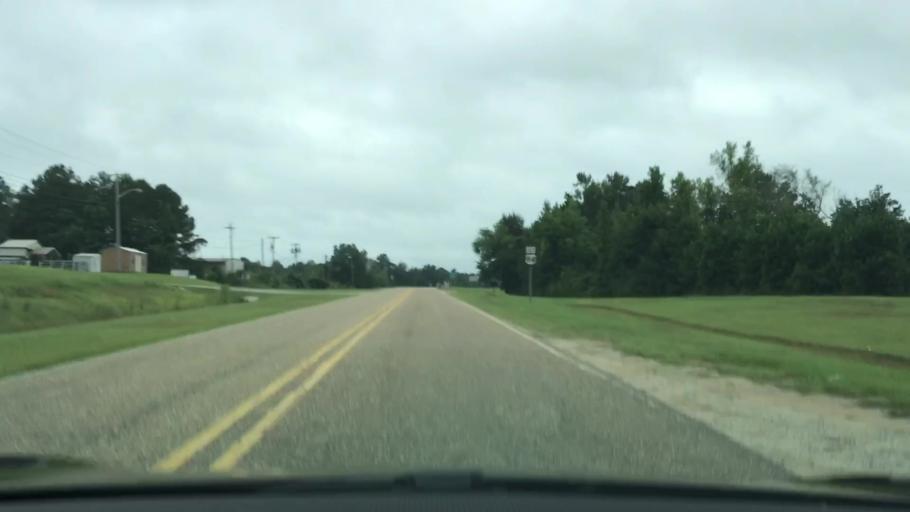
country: US
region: Alabama
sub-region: Coffee County
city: Elba
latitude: 31.4144
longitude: -86.0856
